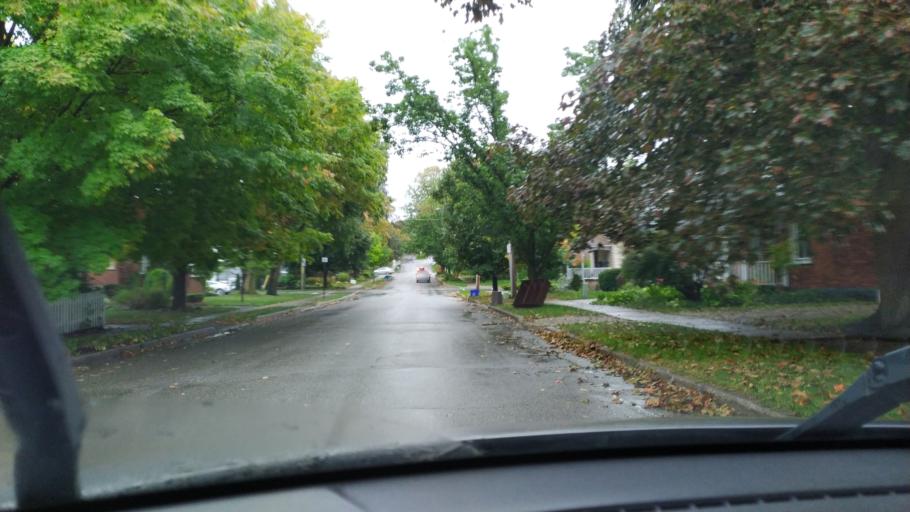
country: CA
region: Ontario
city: Waterloo
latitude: 43.4572
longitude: -80.5199
